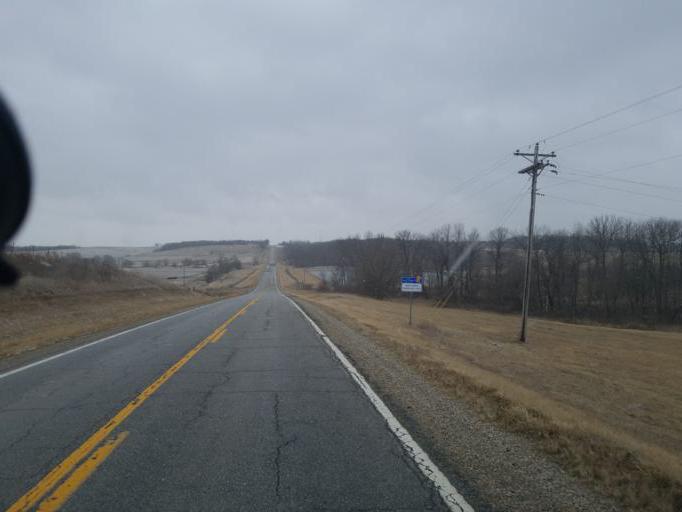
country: US
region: Missouri
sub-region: Putnam County
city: Unionville
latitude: 40.5344
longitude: -93.0185
